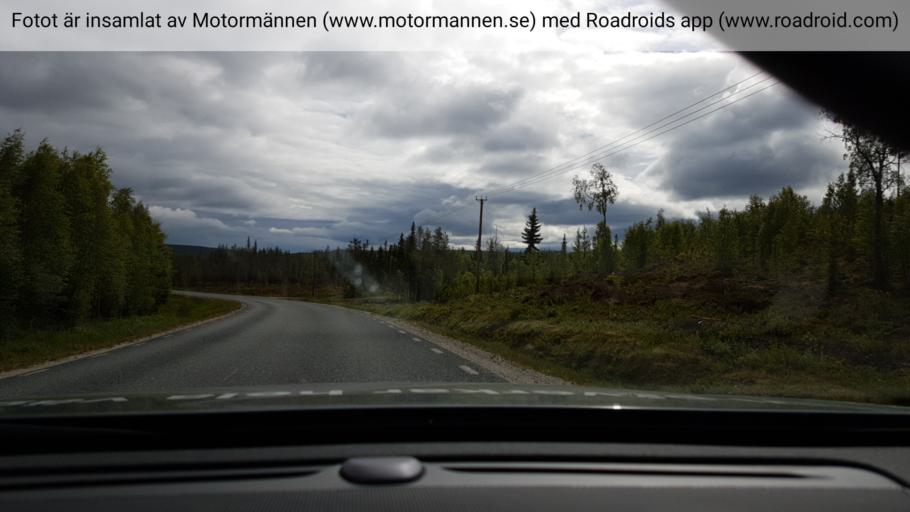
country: SE
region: Vaesterbotten
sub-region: Asele Kommun
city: Insjon
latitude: 64.2887
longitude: 17.6419
